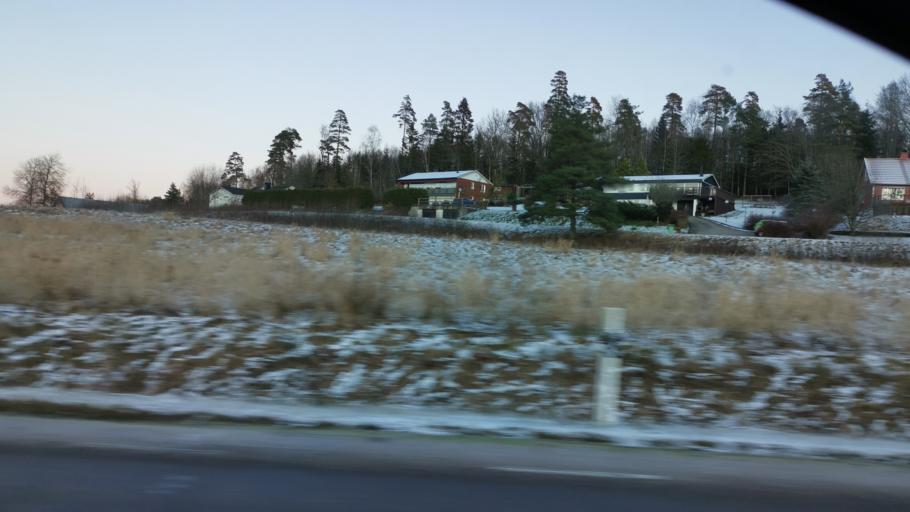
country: SE
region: Vaestra Goetaland
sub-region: Munkedals Kommun
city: Munkedal
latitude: 58.4029
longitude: 11.7432
